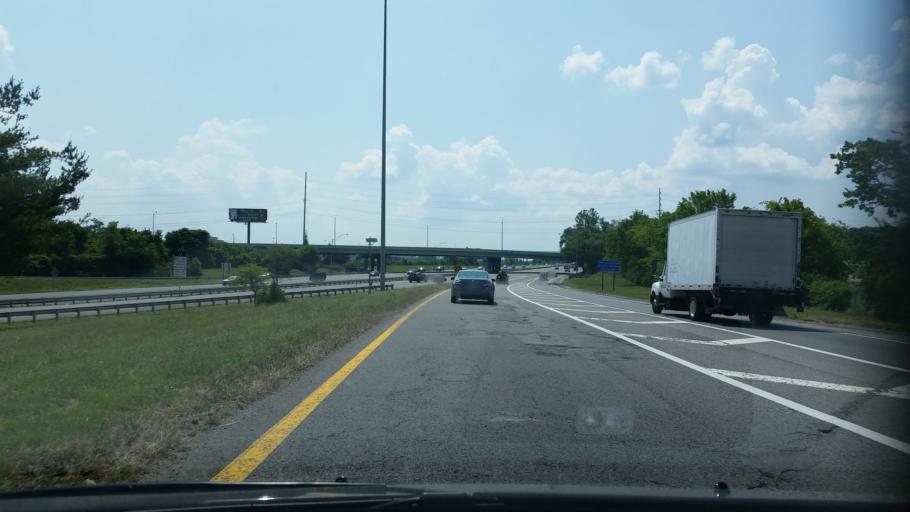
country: US
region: Tennessee
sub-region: Davidson County
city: Oak Hill
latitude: 36.1132
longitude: -86.7733
